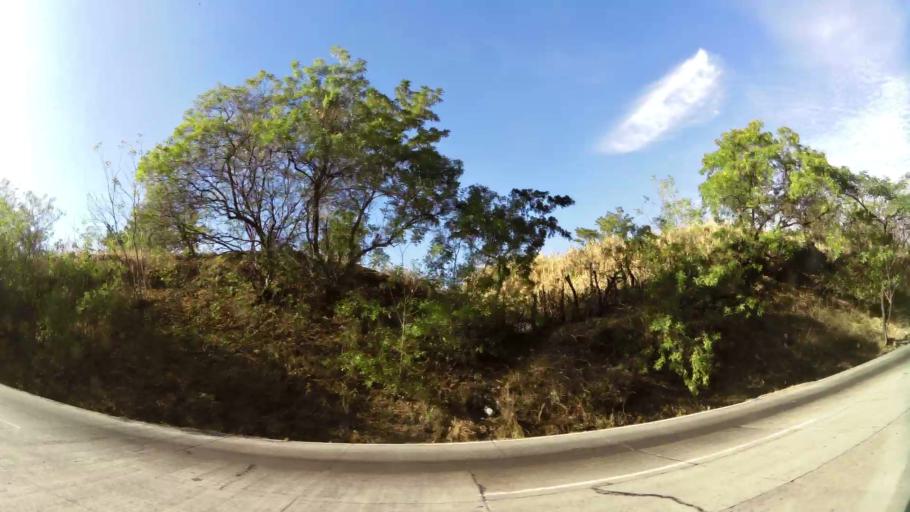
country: SV
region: Santa Ana
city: Texistepeque
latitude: 14.0581
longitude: -89.5094
